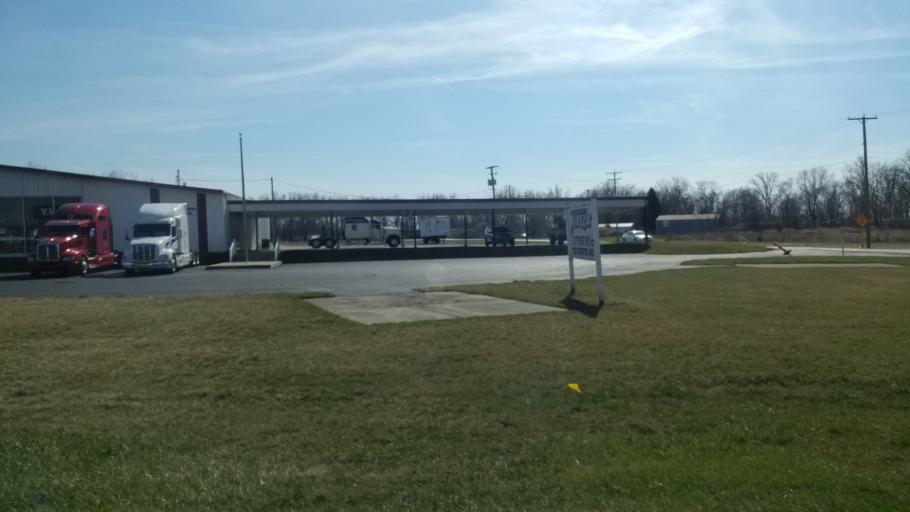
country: US
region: Ohio
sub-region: Hancock County
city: Findlay
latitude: 41.0587
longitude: -83.6769
